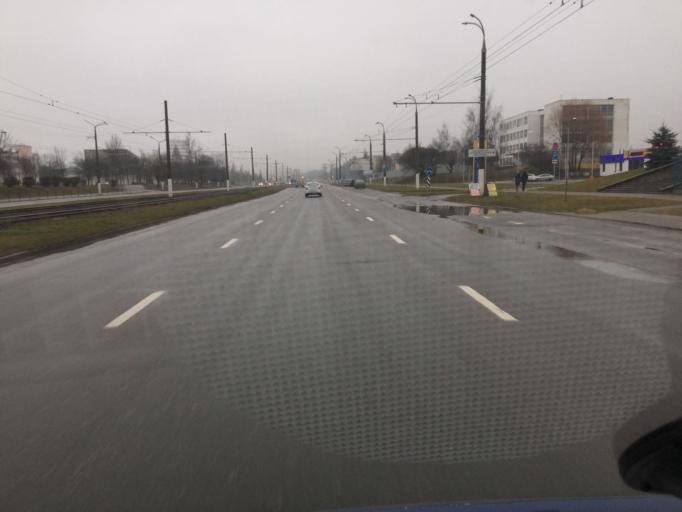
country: BY
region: Vitebsk
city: Vitebsk
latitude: 55.1604
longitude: 30.2362
